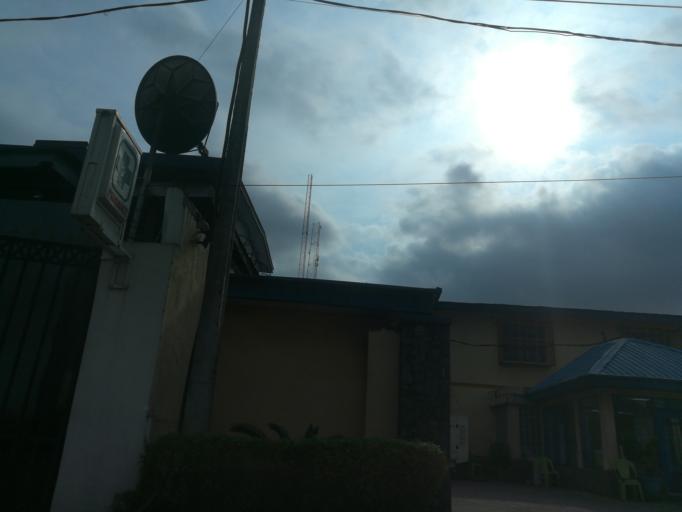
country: NG
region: Lagos
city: Ojota
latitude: 6.5743
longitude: 3.3612
